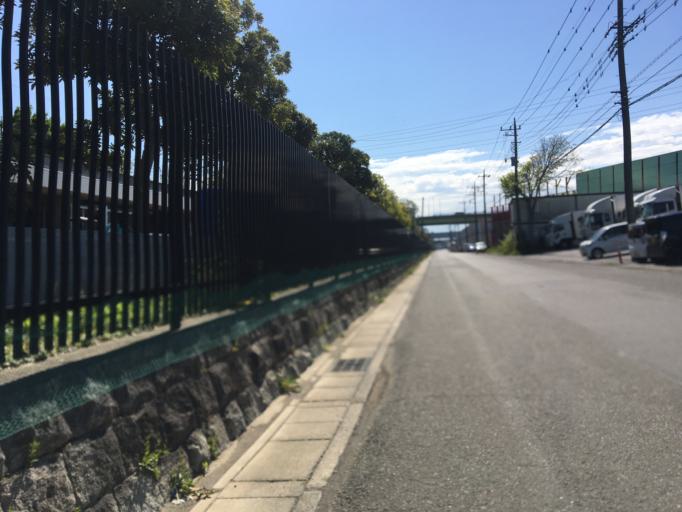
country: JP
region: Saitama
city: Asaka
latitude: 35.8044
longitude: 139.6178
